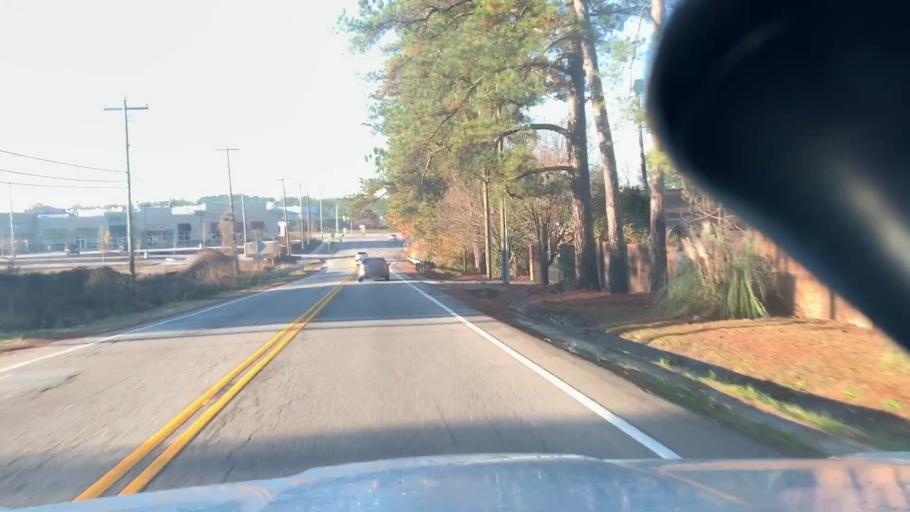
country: US
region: South Carolina
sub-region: Richland County
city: Woodfield
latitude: 34.0254
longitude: -80.9496
